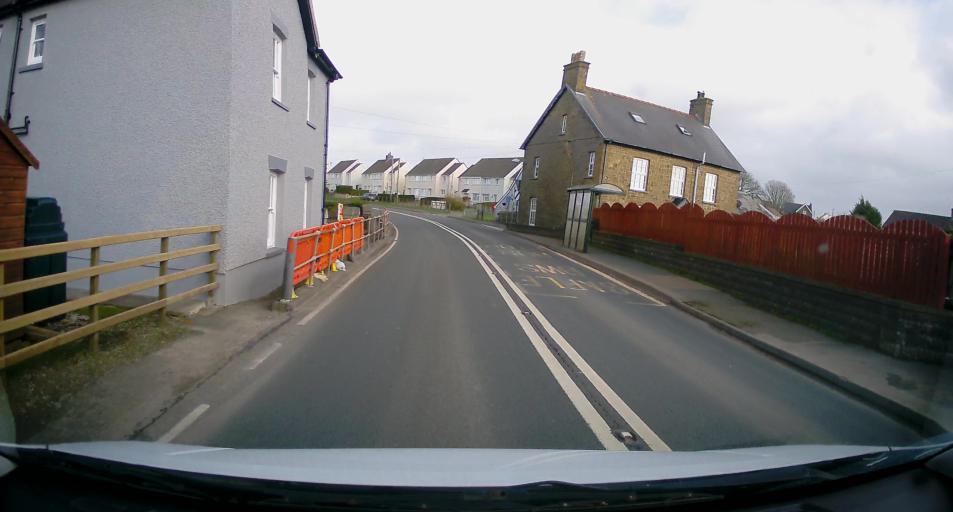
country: GB
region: Wales
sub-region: County of Ceredigion
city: Aberporth
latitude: 52.1158
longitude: -4.5064
